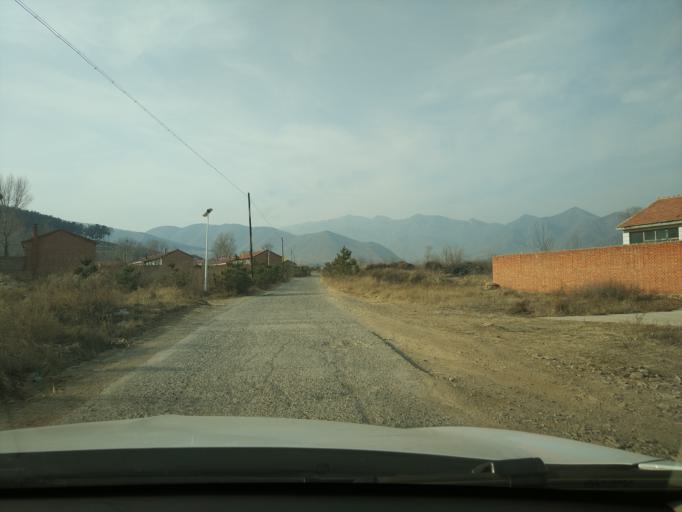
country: CN
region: Hebei
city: Chicheng
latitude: 40.8138
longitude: 115.5342
